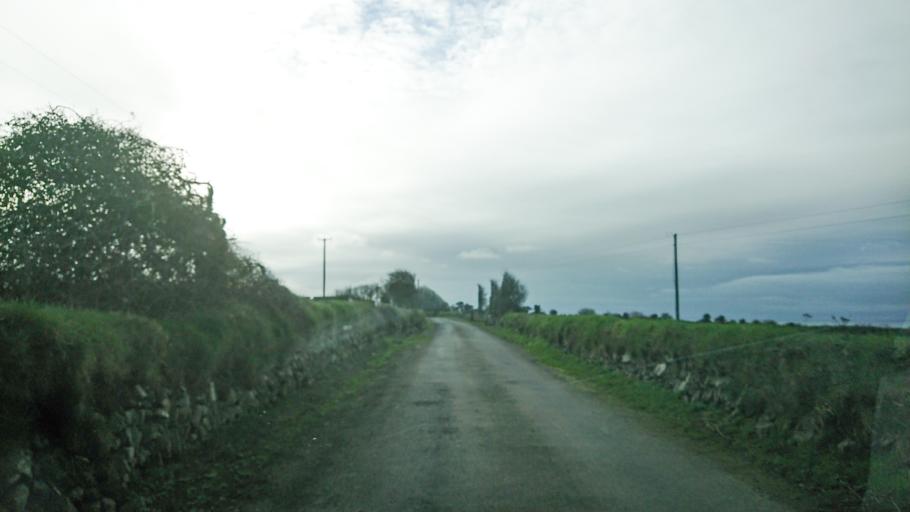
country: IE
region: Munster
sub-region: Waterford
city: Tra Mhor
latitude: 52.1415
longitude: -7.1947
